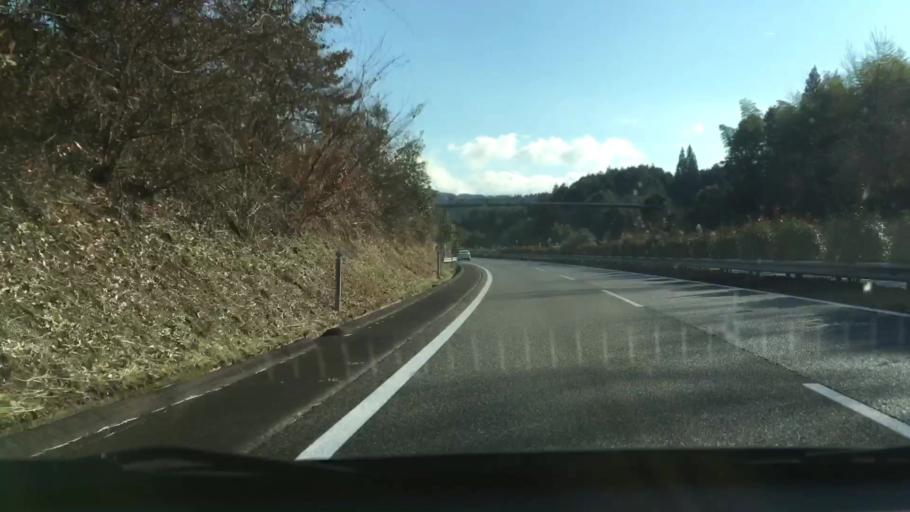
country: JP
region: Kumamoto
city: Hitoyoshi
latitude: 32.1888
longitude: 130.7767
